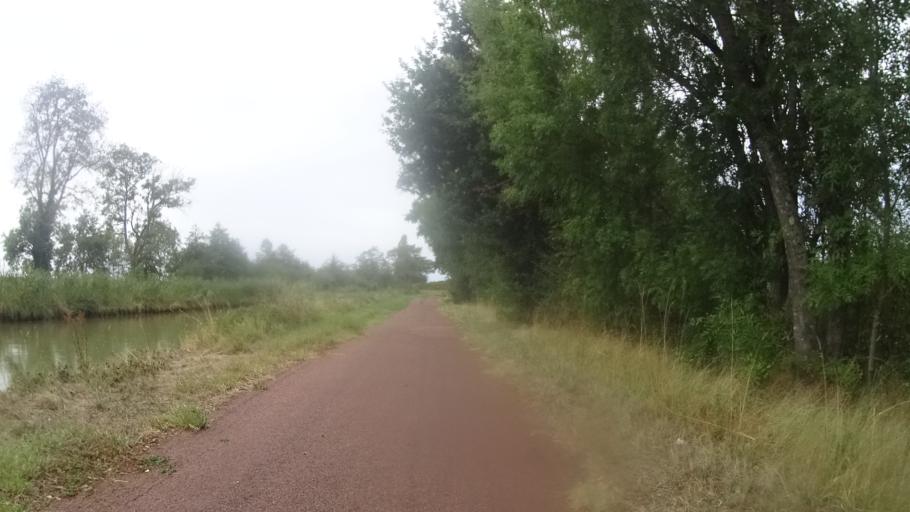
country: FR
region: Bourgogne
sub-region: Departement de la Nievre
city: Imphy
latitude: 46.8561
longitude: 3.2927
